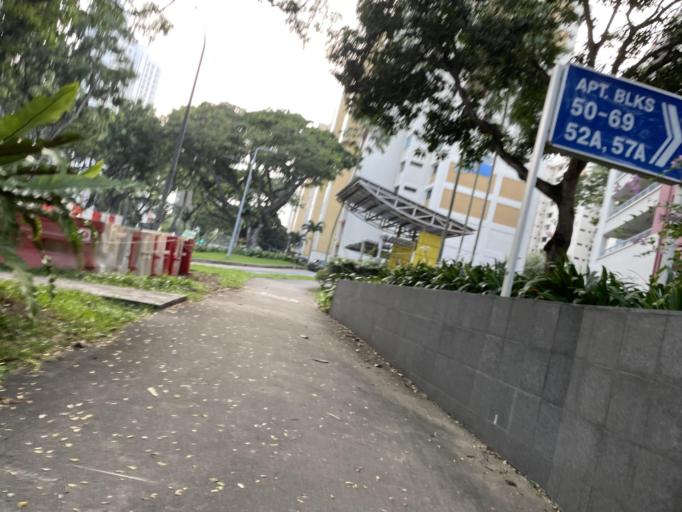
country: SG
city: Singapore
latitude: 1.2729
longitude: 103.8112
